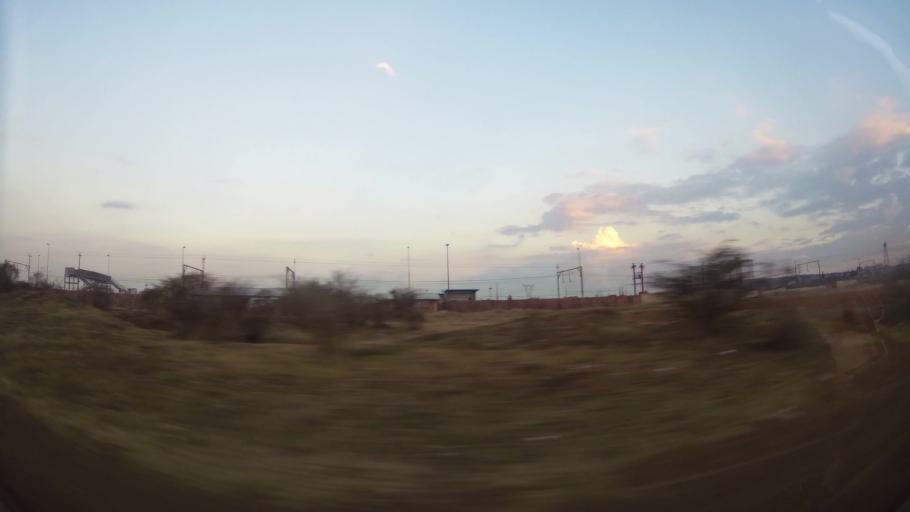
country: ZA
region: Gauteng
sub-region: City of Johannesburg Metropolitan Municipality
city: Orange Farm
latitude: -26.5579
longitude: 27.8773
